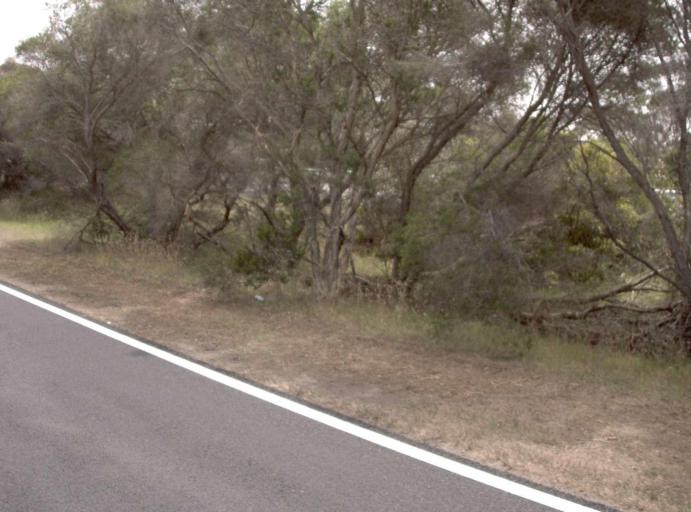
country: AU
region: Victoria
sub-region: Mornington Peninsula
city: Dromana
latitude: -38.3422
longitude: 144.9544
